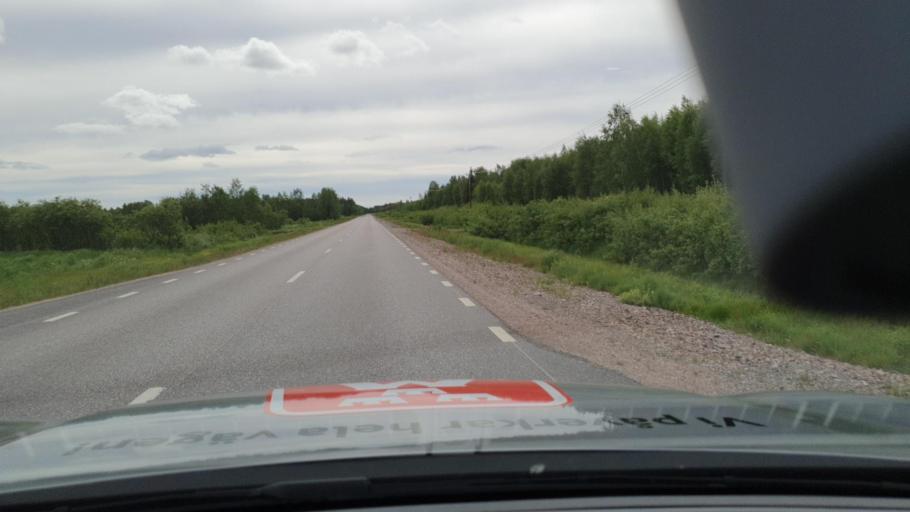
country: SE
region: Norrbotten
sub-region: Kalix Kommun
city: Kalix
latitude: 65.8878
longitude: 23.4718
